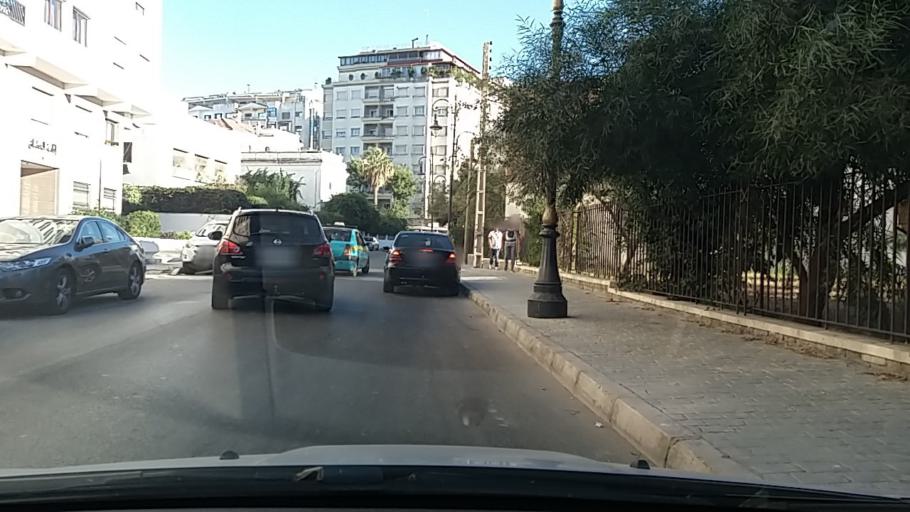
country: MA
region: Tanger-Tetouan
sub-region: Tanger-Assilah
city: Tangier
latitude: 35.7831
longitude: -5.8240
